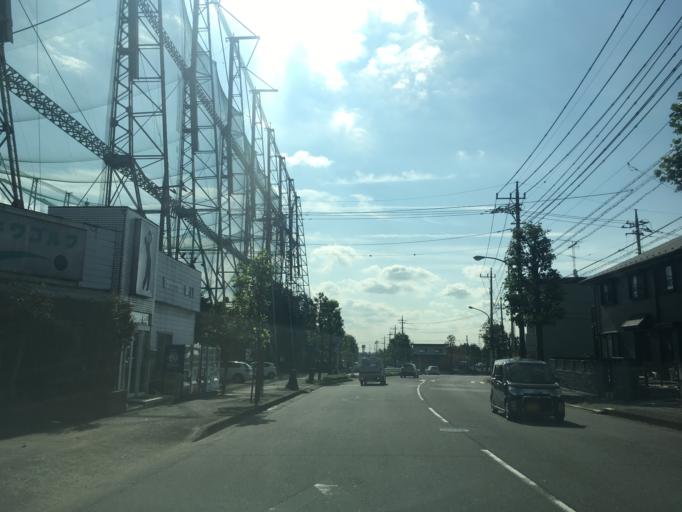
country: JP
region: Tokyo
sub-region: Machida-shi
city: Machida
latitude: 35.5835
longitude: 139.4096
